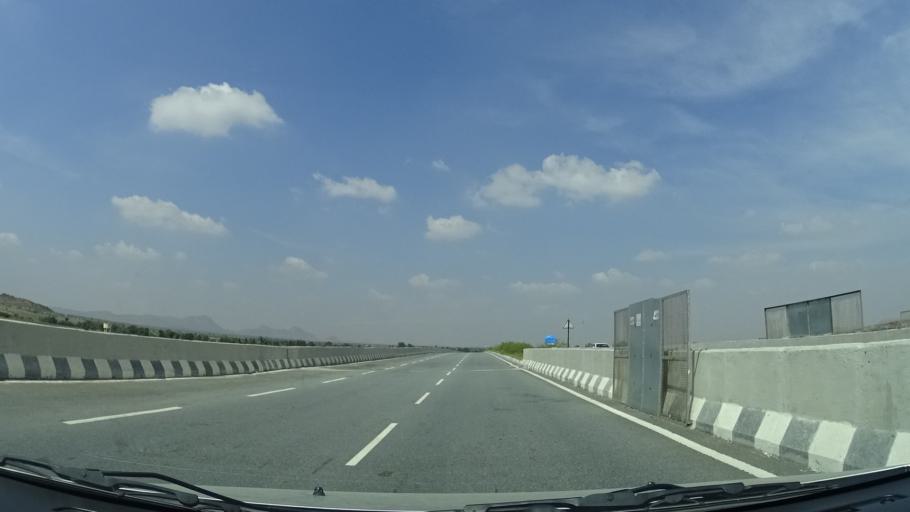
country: IN
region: Andhra Pradesh
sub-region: Anantapur
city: Dharmavaram
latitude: 14.3171
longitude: 77.6364
